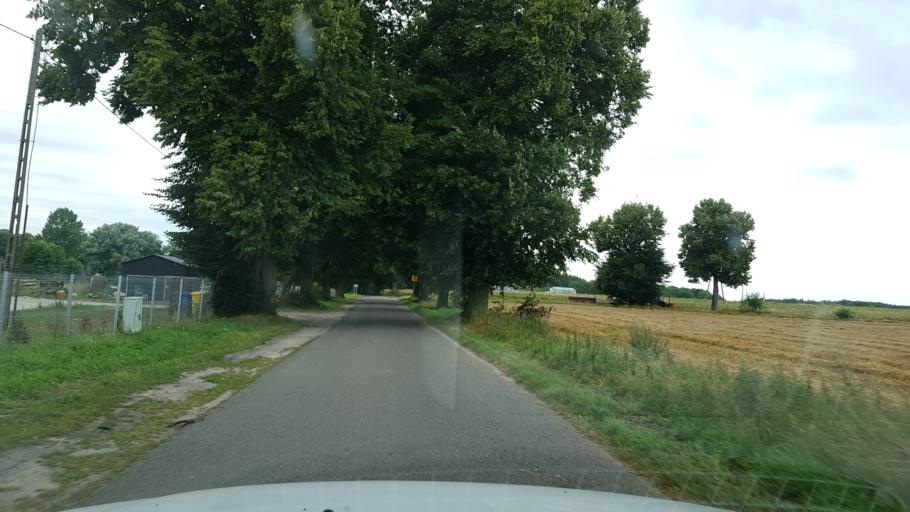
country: PL
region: West Pomeranian Voivodeship
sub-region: Powiat bialogardzki
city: Karlino
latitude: 54.1162
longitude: 15.8476
